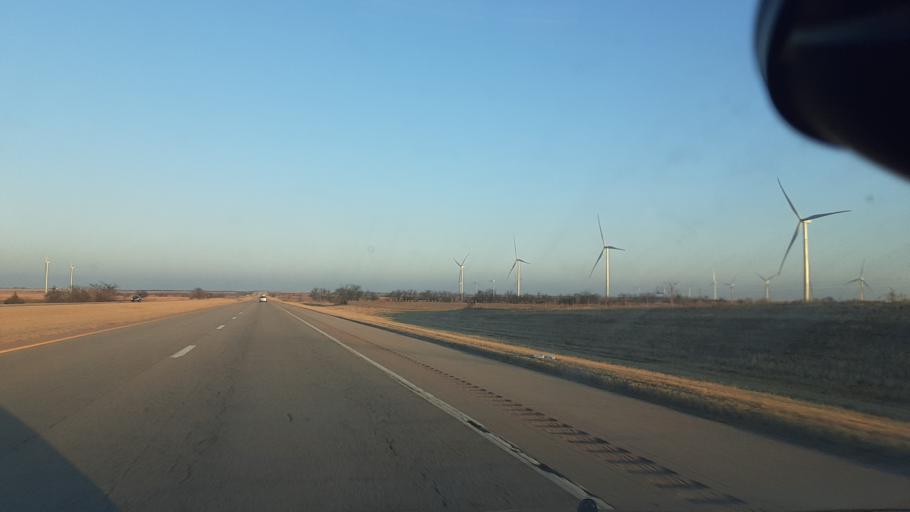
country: US
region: Oklahoma
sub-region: Noble County
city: Perry
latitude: 36.3979
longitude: -97.4233
